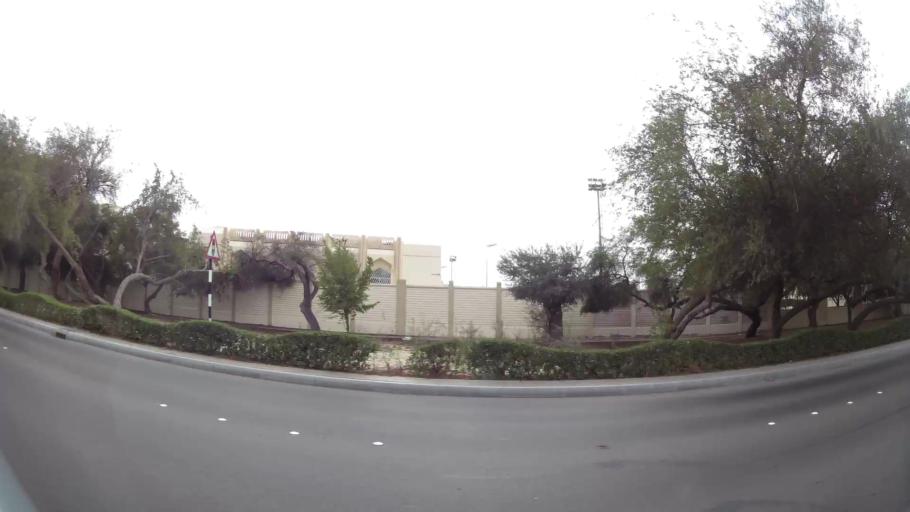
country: AE
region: Abu Dhabi
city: Abu Dhabi
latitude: 24.4618
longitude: 54.3446
